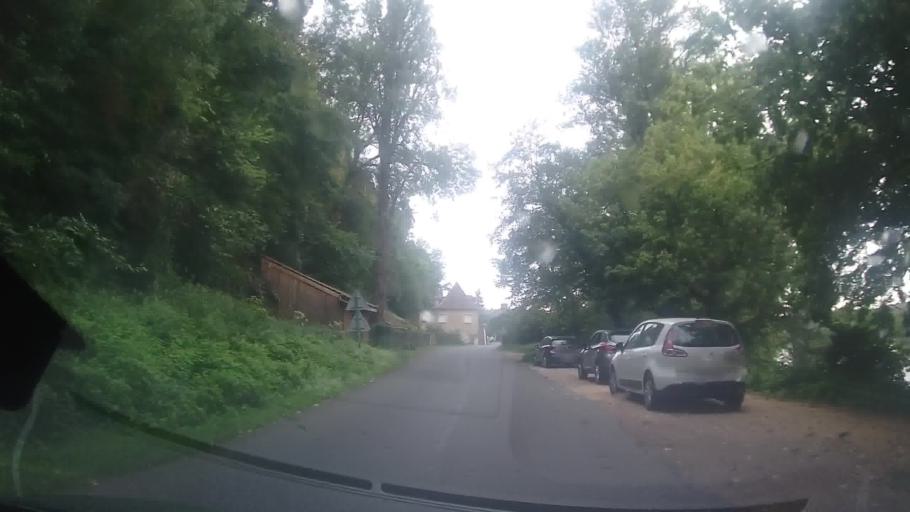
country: FR
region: Aquitaine
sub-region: Departement de la Dordogne
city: Domme
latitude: 44.8056
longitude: 1.2110
